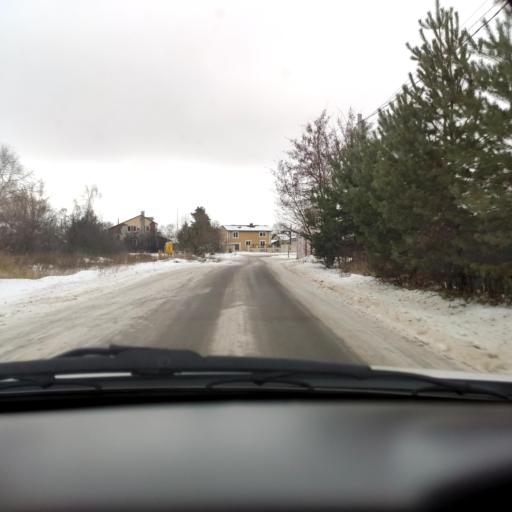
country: RU
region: Voronezj
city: Ramon'
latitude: 51.8874
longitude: 39.2648
